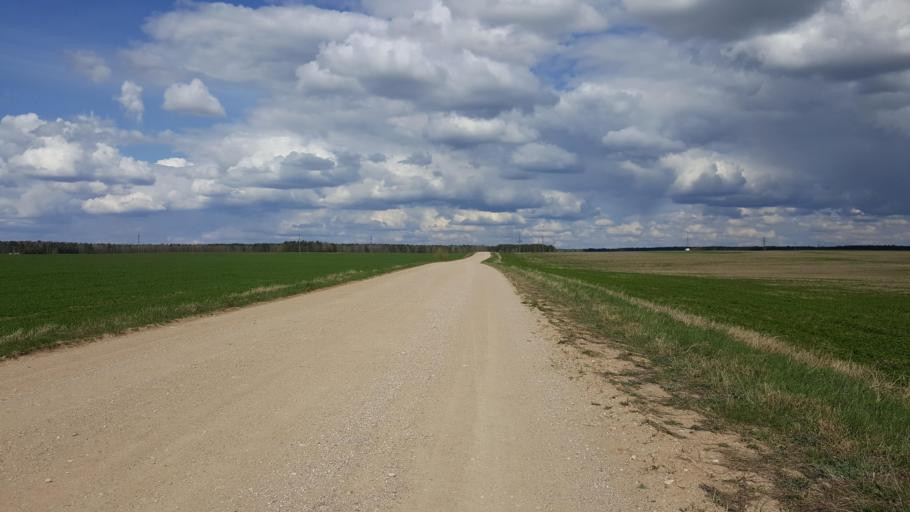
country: BY
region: Brest
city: Kamyanyets
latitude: 52.3744
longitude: 23.6585
